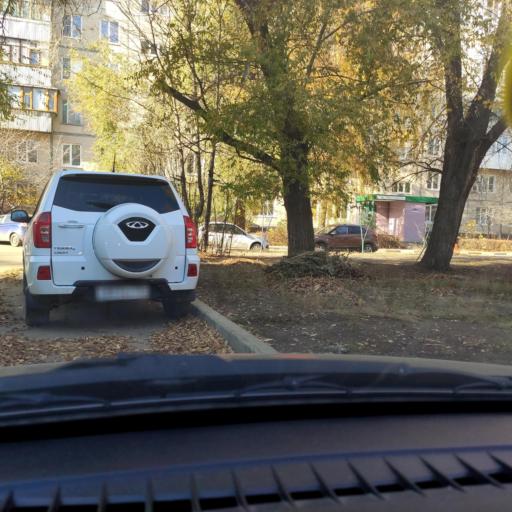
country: RU
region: Samara
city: Tol'yatti
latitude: 53.5288
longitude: 49.3021
